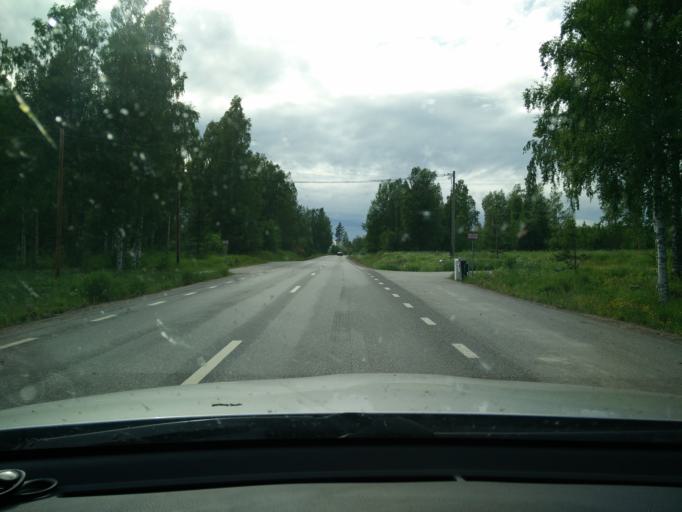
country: SE
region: Gaevleborg
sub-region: Nordanstigs Kommun
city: Bergsjoe
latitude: 62.0848
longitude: 16.7980
